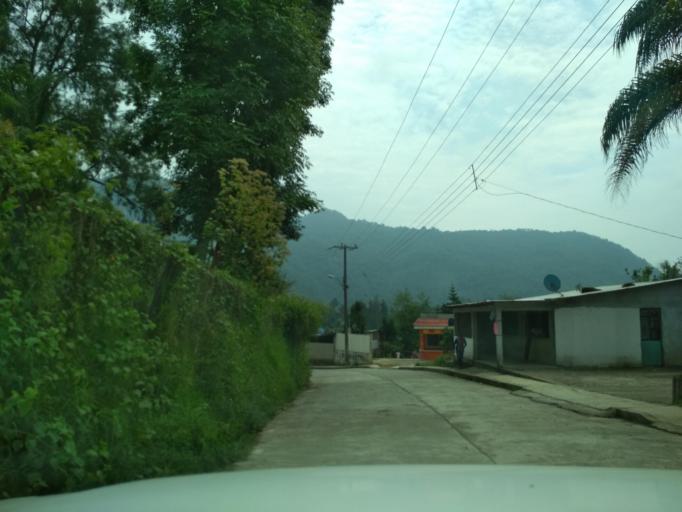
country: MX
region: Veracruz
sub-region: La Perla
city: La Perla
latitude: 18.9298
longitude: -97.1300
